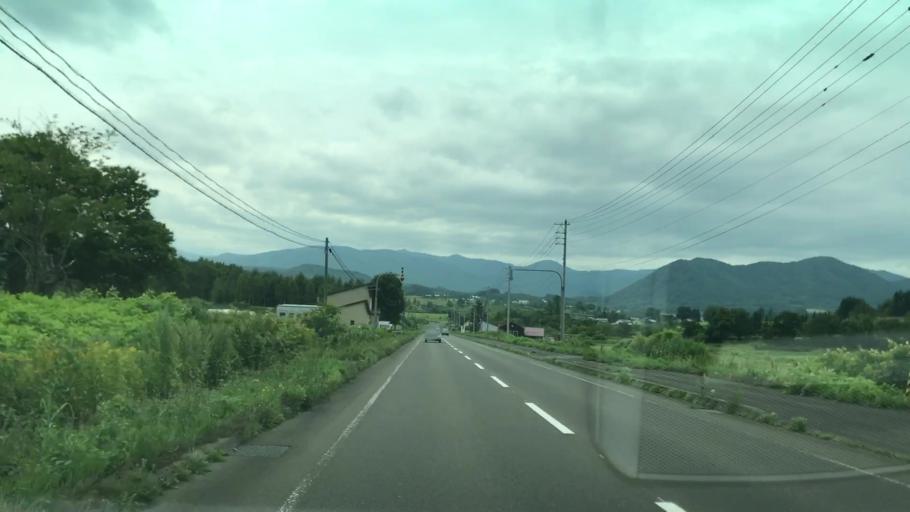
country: JP
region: Hokkaido
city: Yoichi
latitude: 43.1050
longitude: 140.8234
